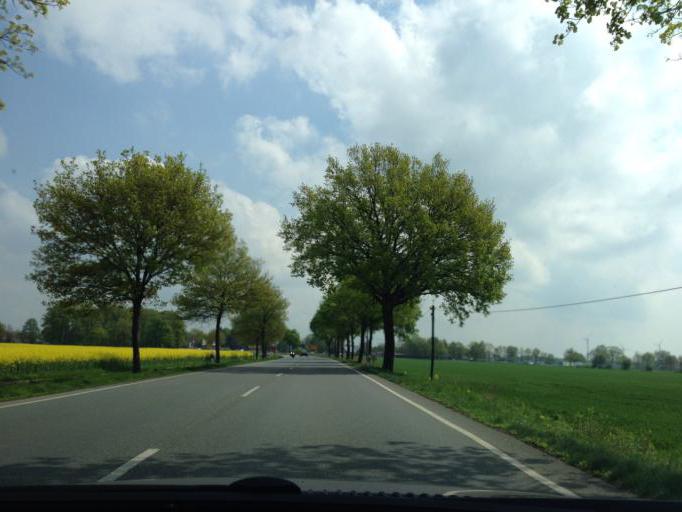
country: DE
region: Lower Saxony
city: Eicklingen
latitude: 52.5493
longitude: 10.1679
